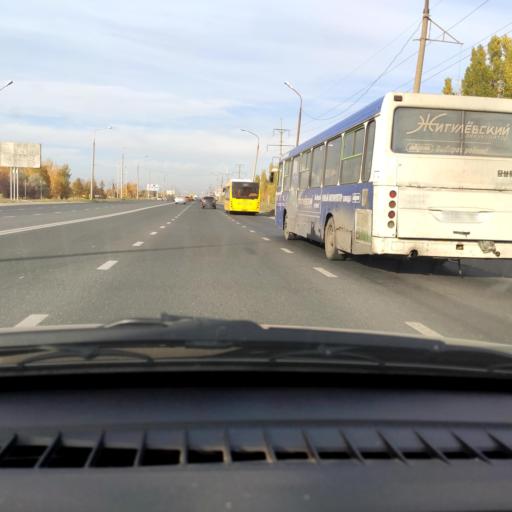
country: RU
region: Samara
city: Tol'yatti
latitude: 53.5582
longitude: 49.2889
